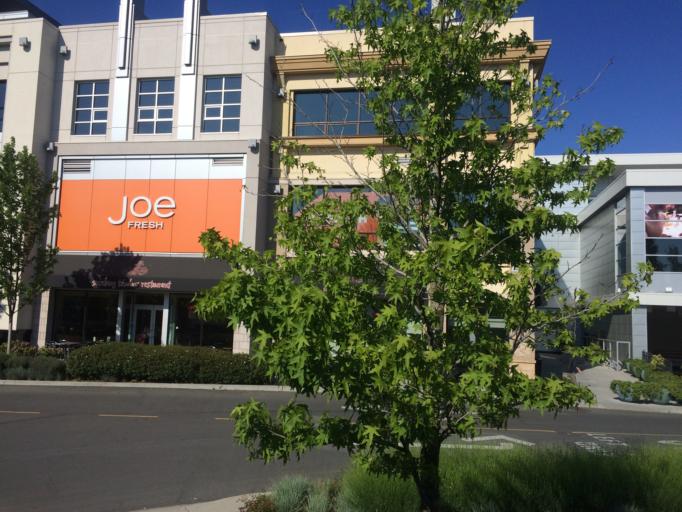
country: CA
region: British Columbia
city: Victoria
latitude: 48.4546
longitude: -123.3765
